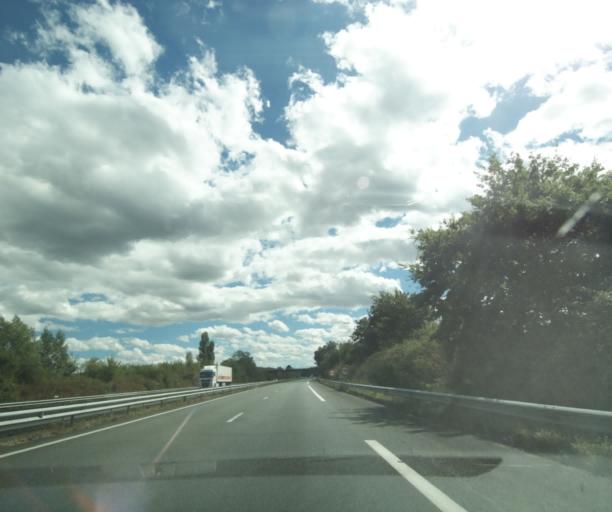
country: FR
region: Aquitaine
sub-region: Departement de la Gironde
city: Gironde-sur-Dropt
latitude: 44.5278
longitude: -0.0903
